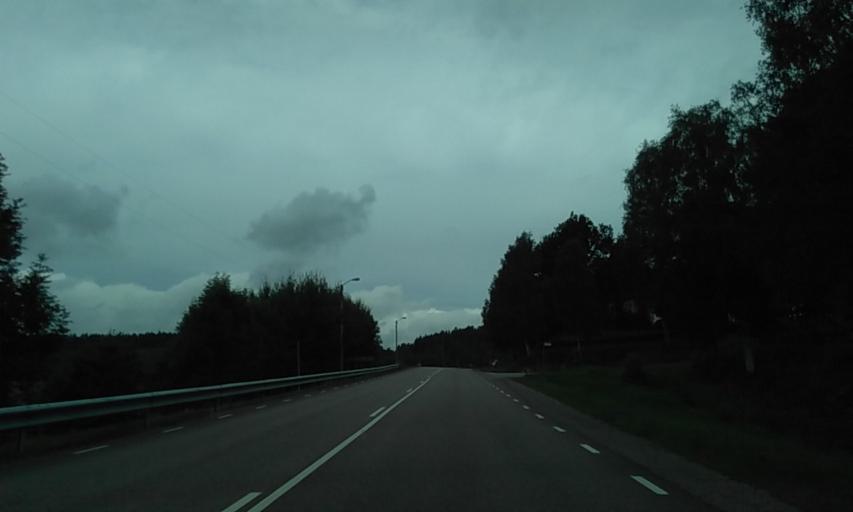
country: SE
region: Vaestra Goetaland
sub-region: Bollebygds Kommun
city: Bollebygd
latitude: 57.6724
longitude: 12.5551
